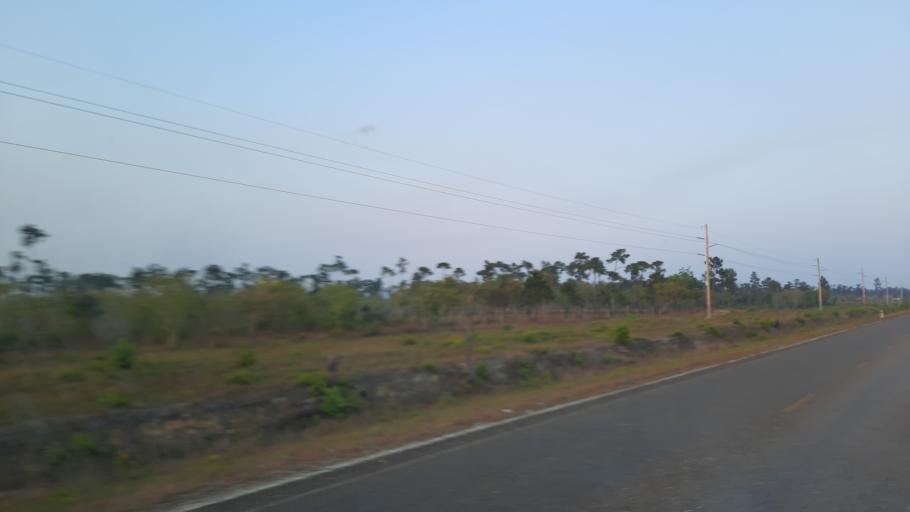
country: BZ
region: Stann Creek
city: Placencia
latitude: 16.5320
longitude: -88.4655
